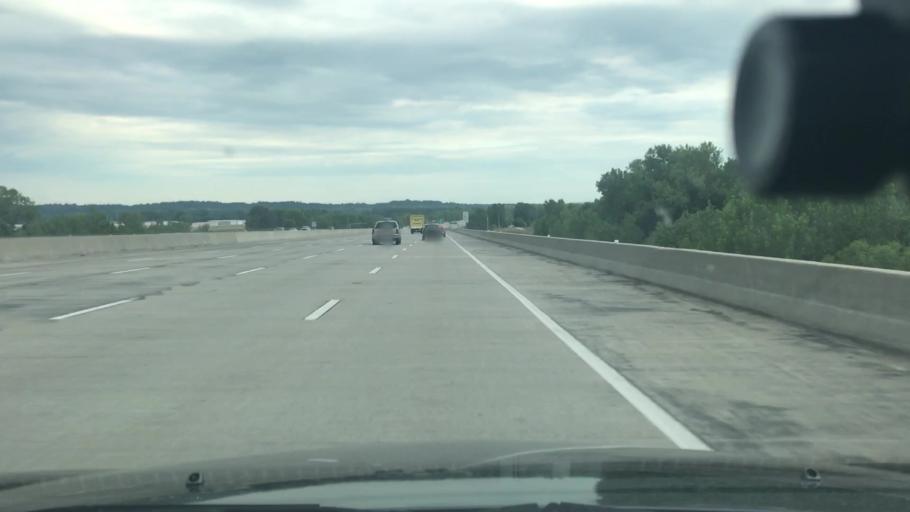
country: US
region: Missouri
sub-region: Saint Charles County
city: Saint Charles
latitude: 38.7336
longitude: -90.5202
